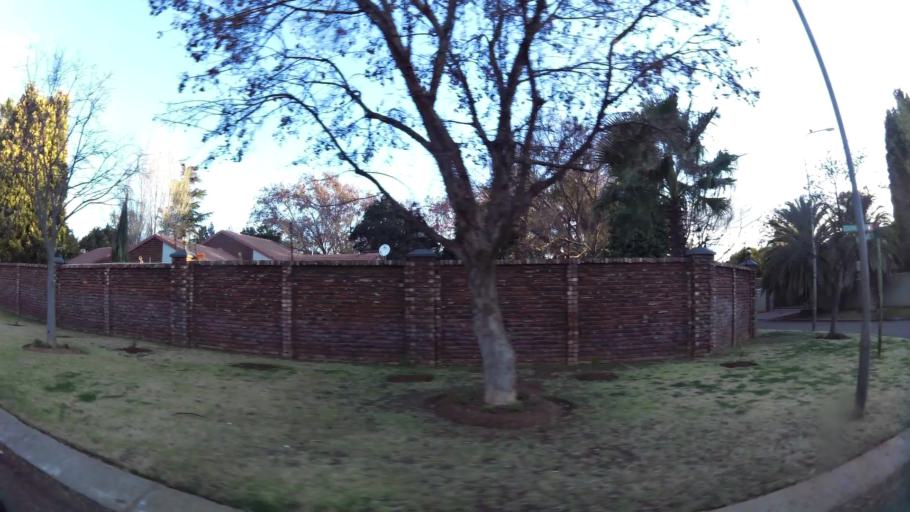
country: ZA
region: North-West
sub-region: Dr Kenneth Kaunda District Municipality
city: Potchefstroom
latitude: -26.6779
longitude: 27.1110
